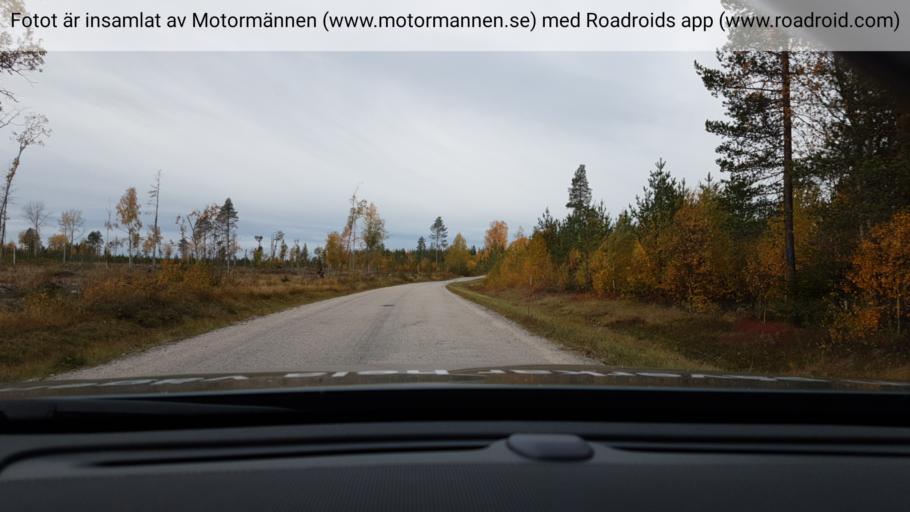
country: SE
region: Norrbotten
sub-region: Overkalix Kommun
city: OEverkalix
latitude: 66.2576
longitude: 23.0688
